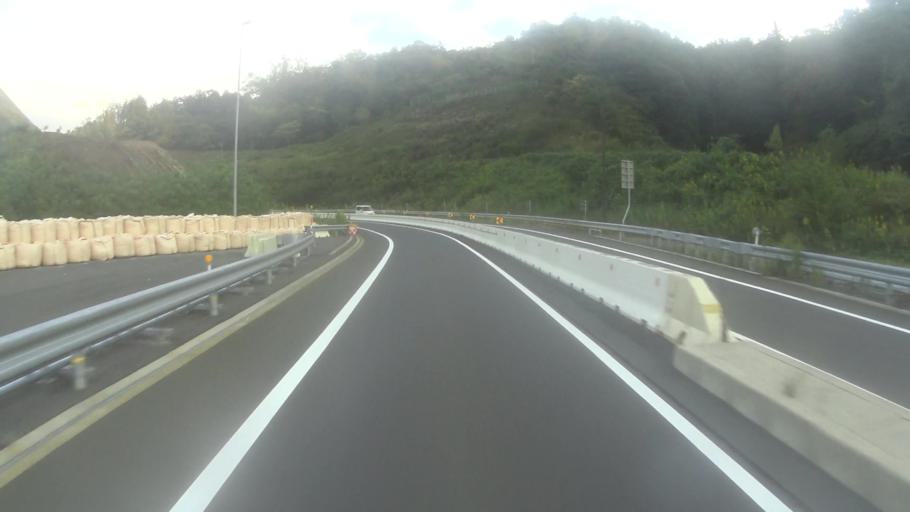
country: JP
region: Kyoto
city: Miyazu
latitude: 35.5496
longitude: 135.1426
